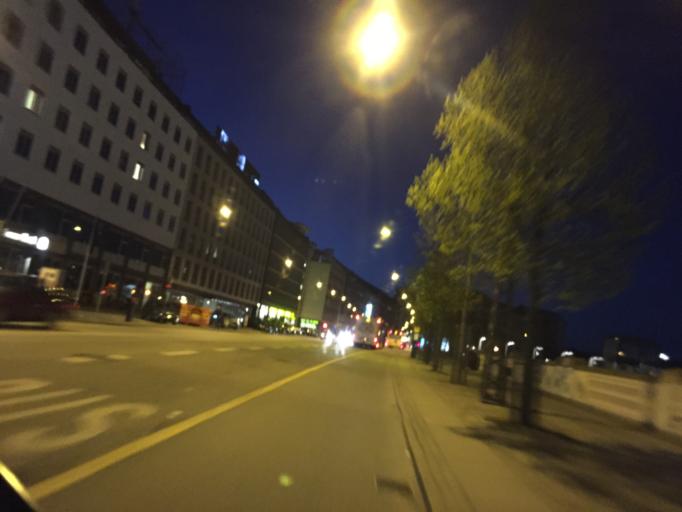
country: DK
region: Capital Region
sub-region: Kobenhavn
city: Copenhagen
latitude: 55.6762
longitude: 12.5621
